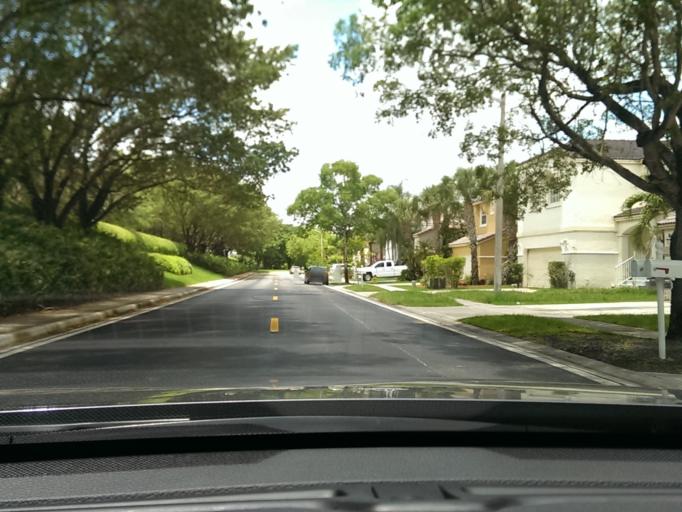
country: US
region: Florida
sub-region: Broward County
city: Sunshine Ranches
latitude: 26.0082
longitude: -80.3475
